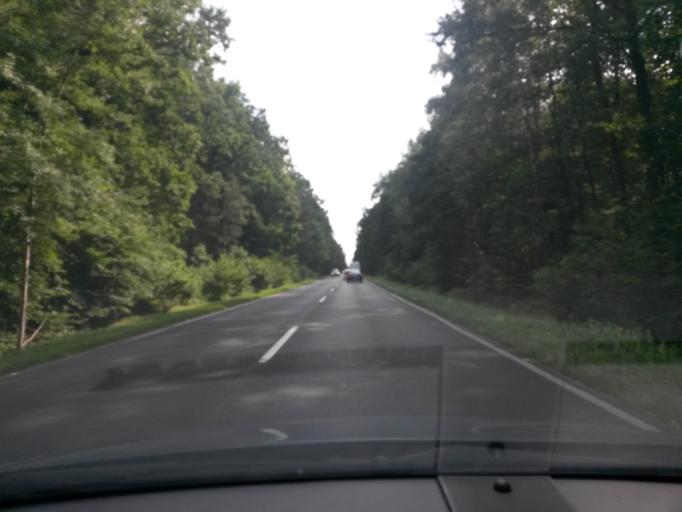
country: PL
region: Greater Poland Voivodeship
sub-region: Powiat poznanski
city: Kornik
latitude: 52.2019
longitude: 17.0648
